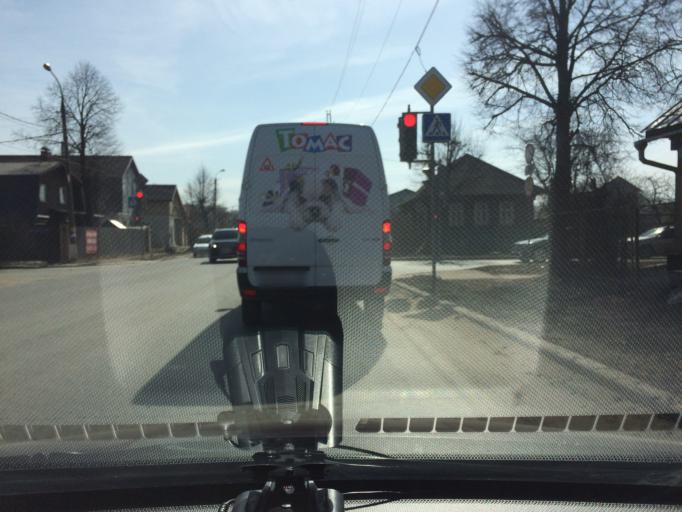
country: RU
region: Mariy-El
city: Yoshkar-Ola
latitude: 56.6467
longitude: 47.9063
